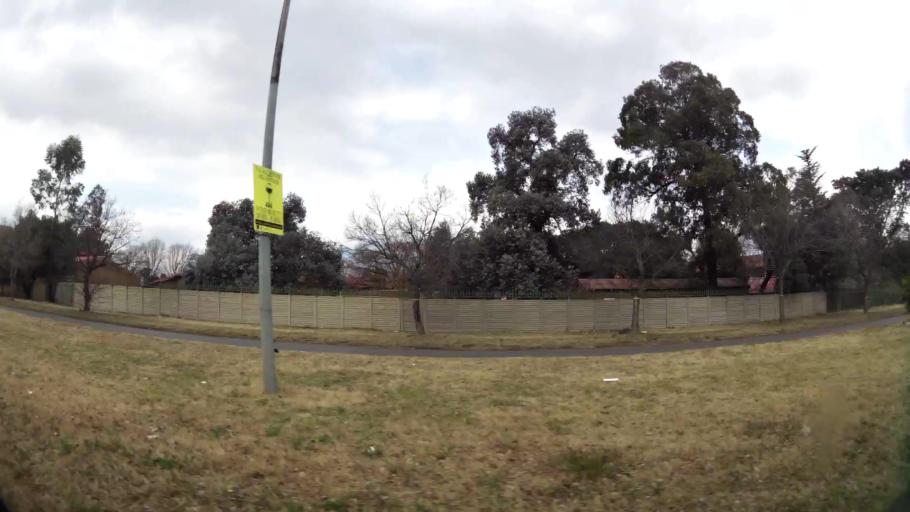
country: ZA
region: Gauteng
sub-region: Sedibeng District Municipality
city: Vanderbijlpark
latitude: -26.7129
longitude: 27.8245
